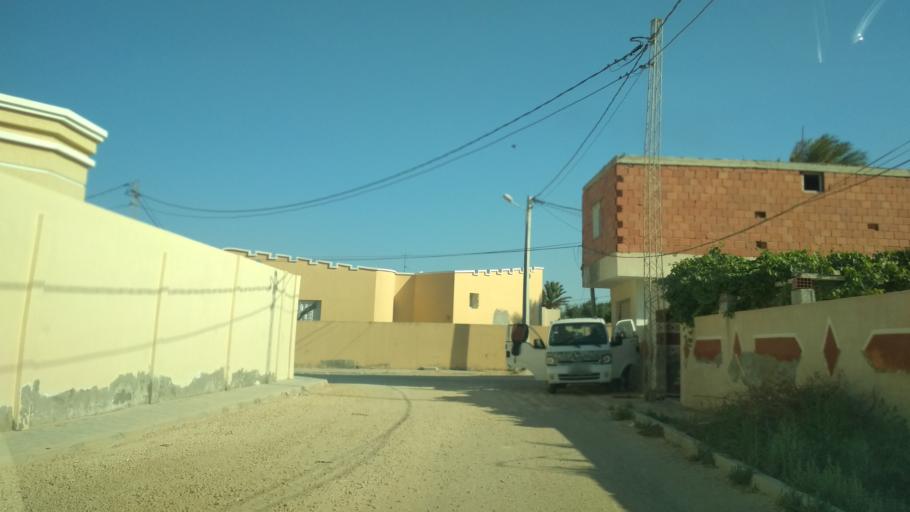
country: TN
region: Qabis
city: Gabes
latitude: 33.9496
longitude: 10.0642
